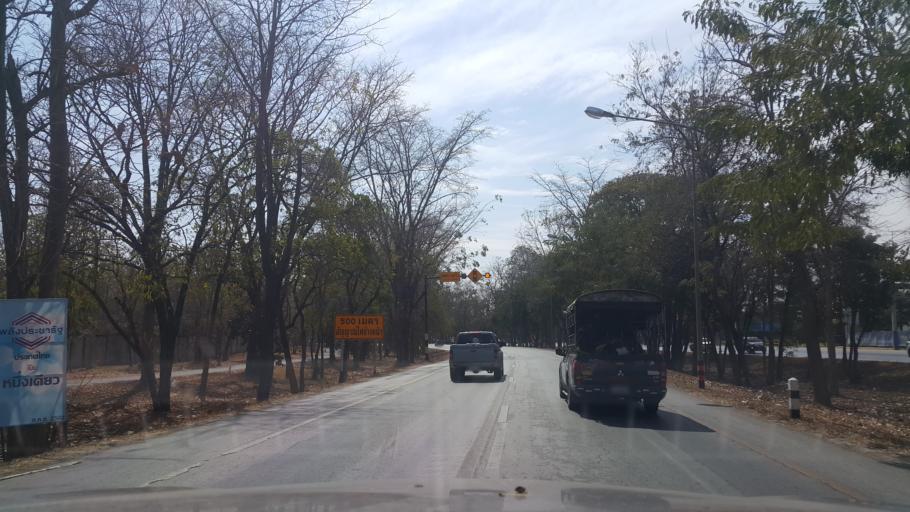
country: TH
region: Nakhon Ratchasima
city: Nakhon Ratchasima
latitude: 14.9356
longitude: 102.0543
